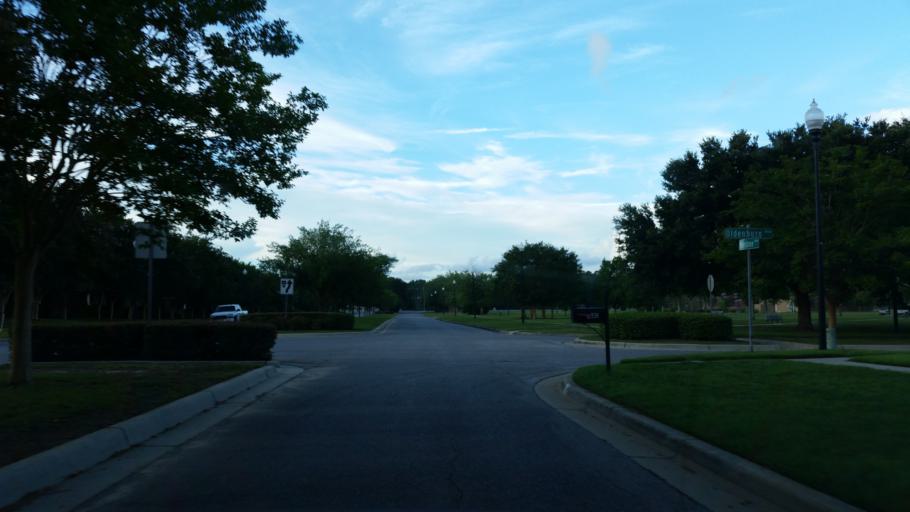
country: US
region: Florida
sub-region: Escambia County
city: Ensley
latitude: 30.5368
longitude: -87.3079
